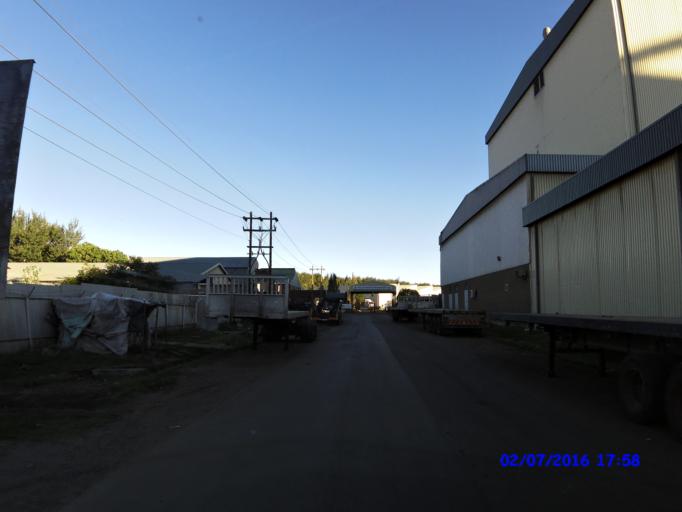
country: LS
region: Maseru
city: Maseru
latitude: -29.2954
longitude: 27.4818
